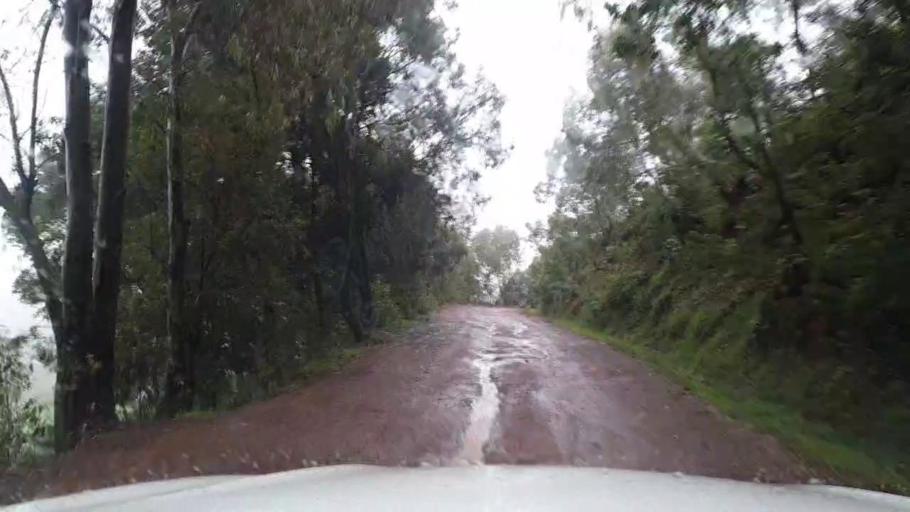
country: RW
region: Kigali
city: Kigali
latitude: -1.7649
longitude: 29.9937
